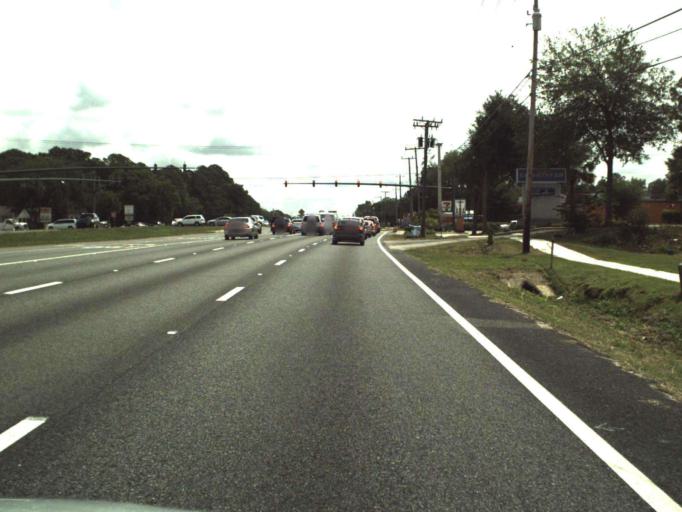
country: US
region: Florida
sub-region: Seminole County
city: Sanford
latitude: 28.8115
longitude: -81.3242
